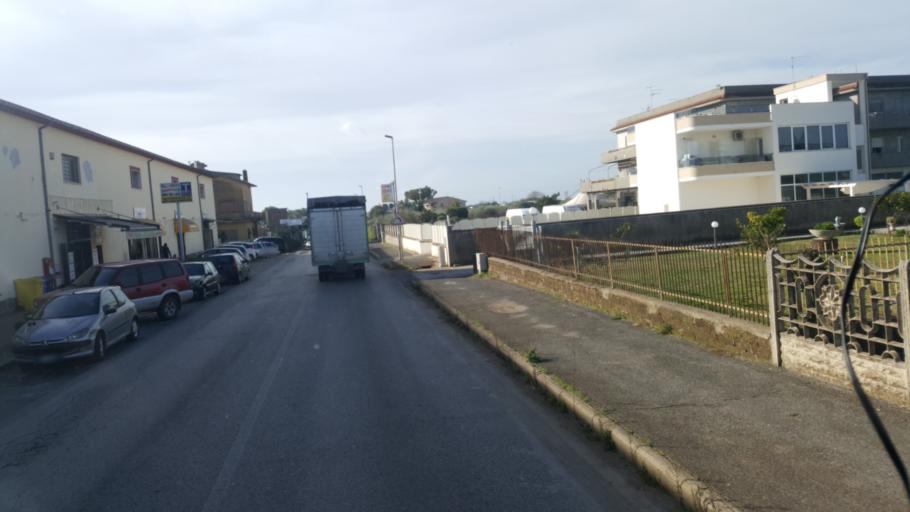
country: IT
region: Latium
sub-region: Provincia di Latina
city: Casalazzara
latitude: 41.6274
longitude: 12.5915
